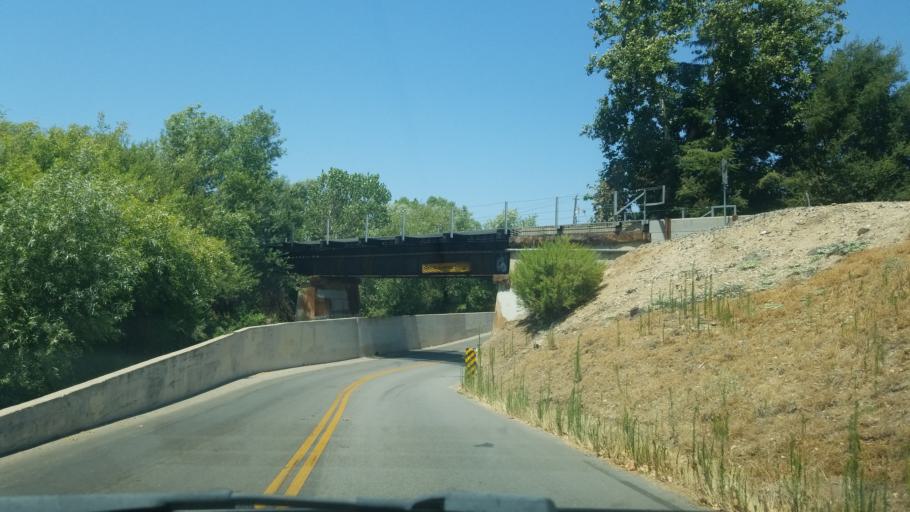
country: US
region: California
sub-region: San Luis Obispo County
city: Atascadero
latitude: 35.5006
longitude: -120.6623
